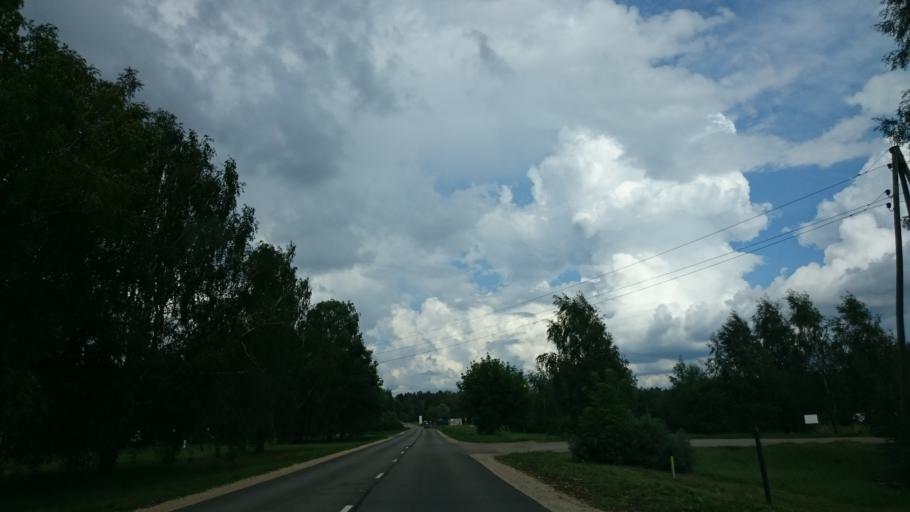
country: LV
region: Salaspils
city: Salaspils
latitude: 56.8655
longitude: 24.3745
